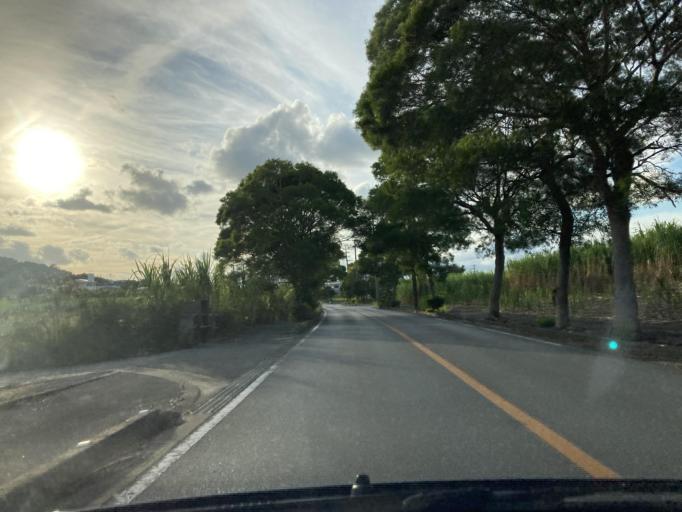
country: JP
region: Okinawa
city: Itoman
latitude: 26.1353
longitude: 127.7150
